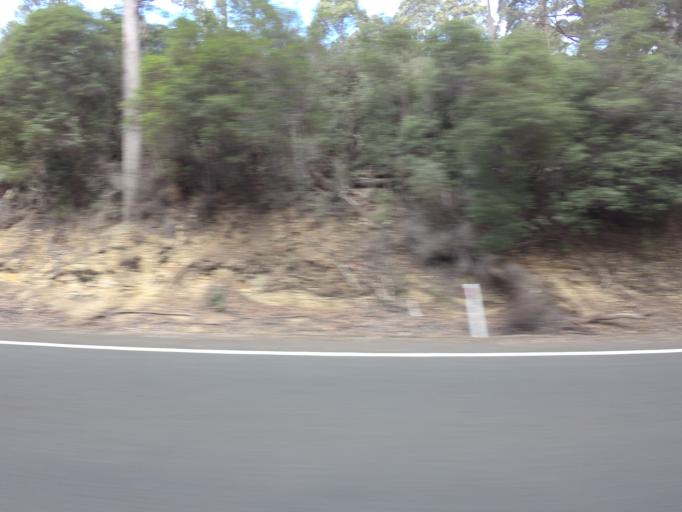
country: AU
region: Tasmania
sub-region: Meander Valley
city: Deloraine
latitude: -41.6551
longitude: 146.7152
